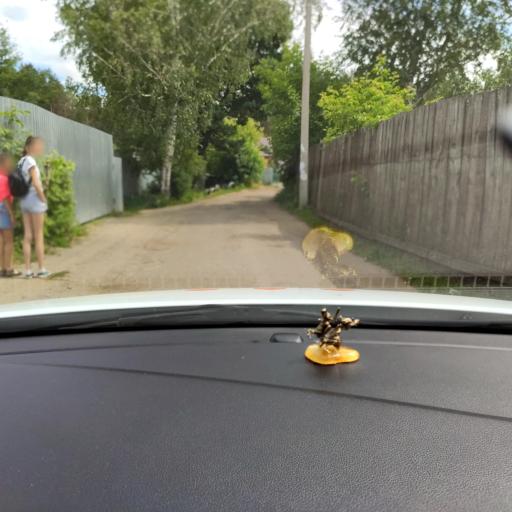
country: RU
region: Tatarstan
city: Staroye Arakchino
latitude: 55.8897
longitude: 49.0432
